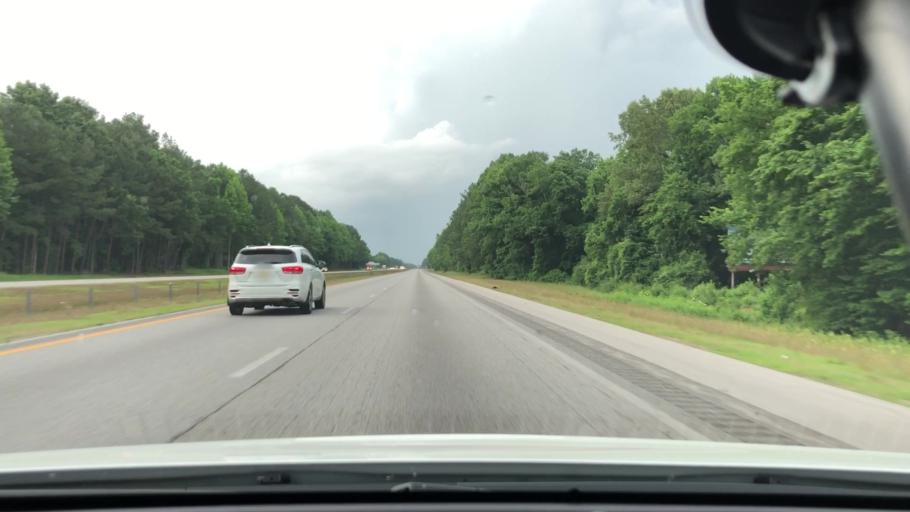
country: US
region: North Carolina
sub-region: Halifax County
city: Enfield
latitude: 36.2520
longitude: -77.7271
